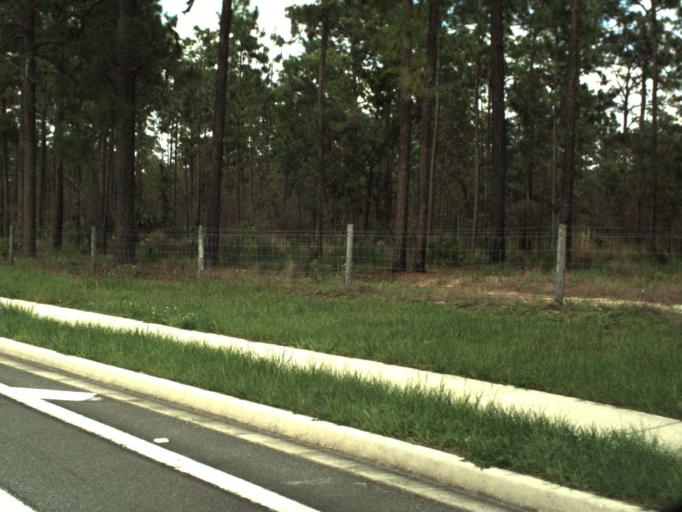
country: US
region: Florida
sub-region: Marion County
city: Ocala
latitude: 29.2025
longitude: -82.0536
